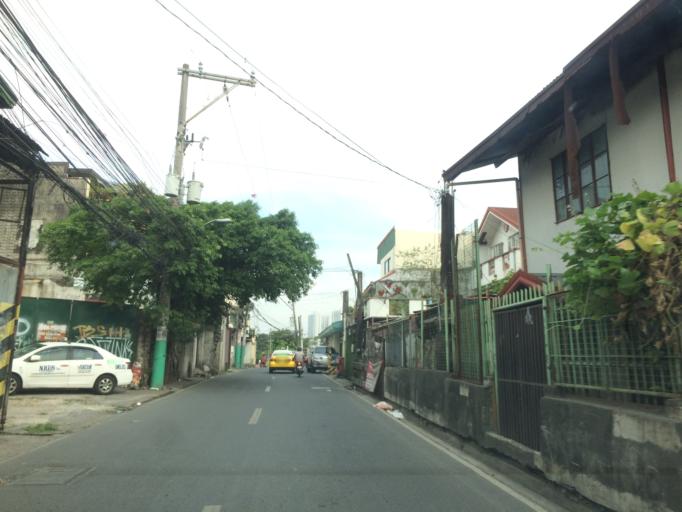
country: PH
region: Calabarzon
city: Bagong Pagasa
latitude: 14.6686
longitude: 121.0160
